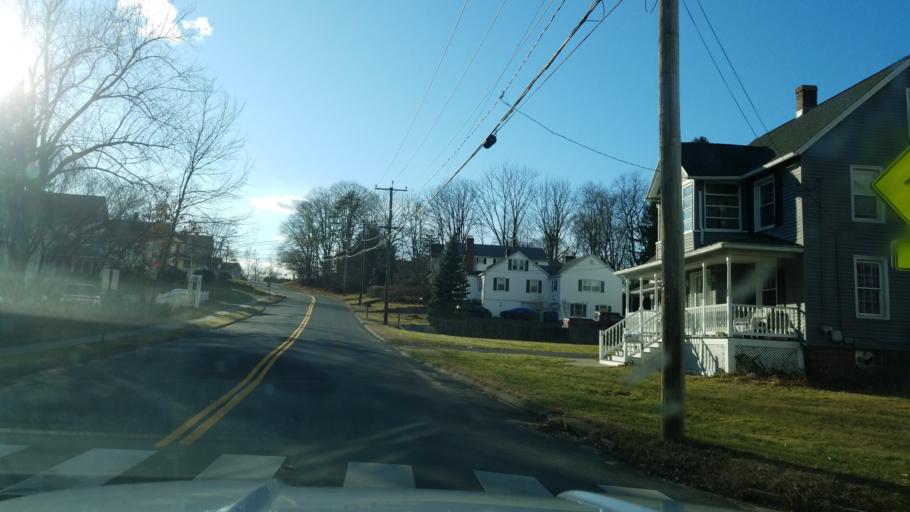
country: US
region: Connecticut
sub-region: Middlesex County
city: Middletown
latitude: 41.5434
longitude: -72.6404
